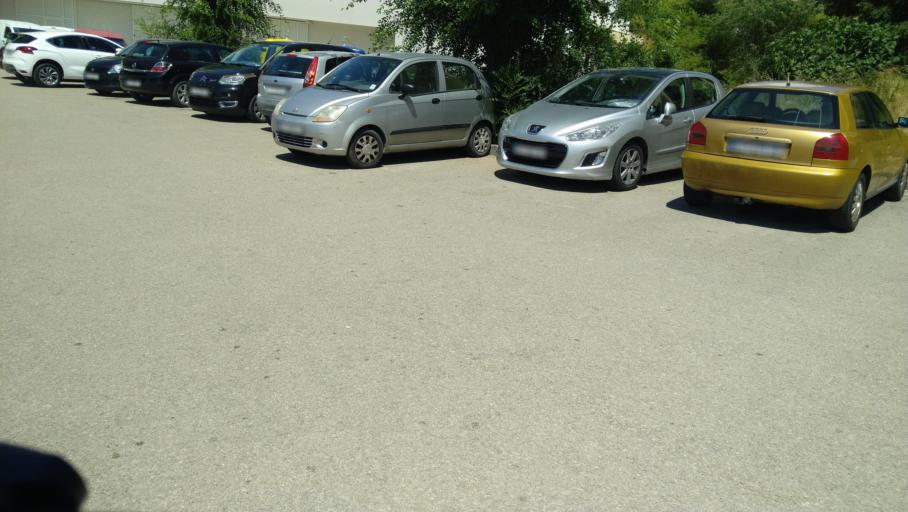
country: HR
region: Sibensko-Kniniska
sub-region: Grad Sibenik
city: Sibenik
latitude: 43.7234
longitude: 15.9094
